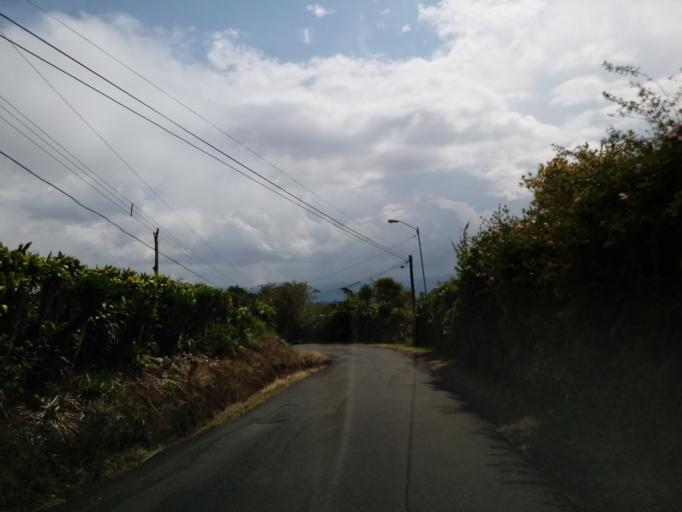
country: CR
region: Heredia
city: Angeles
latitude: 10.0267
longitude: -84.0319
